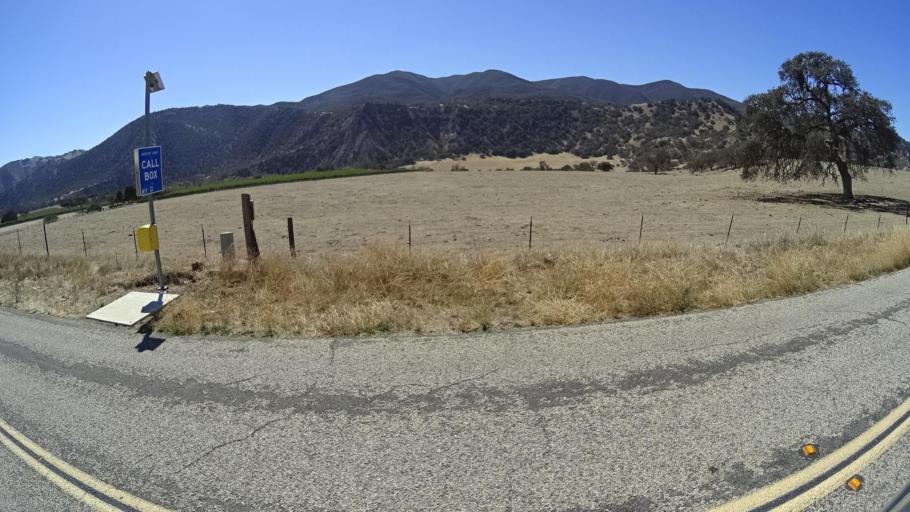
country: US
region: California
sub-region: Monterey County
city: Greenfield
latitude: 36.2684
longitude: -121.3750
